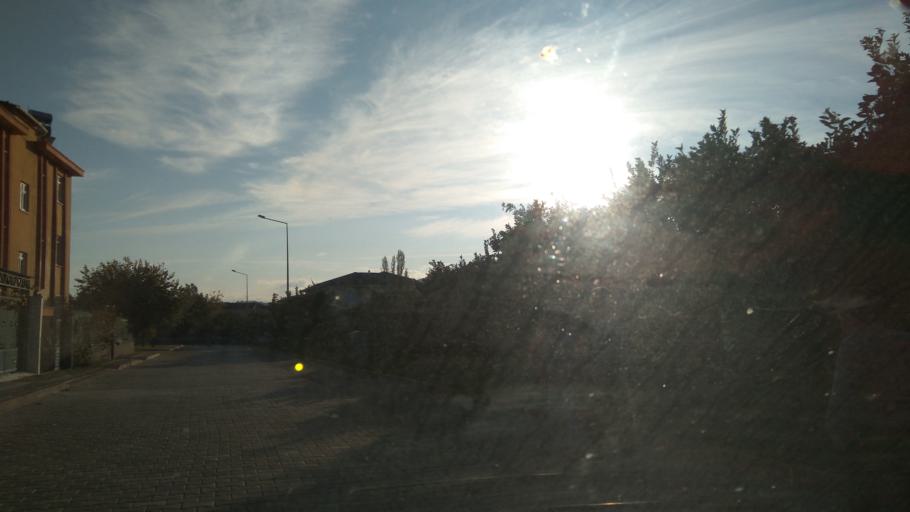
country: TR
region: Antalya
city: Kemer
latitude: 36.5669
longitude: 30.5604
